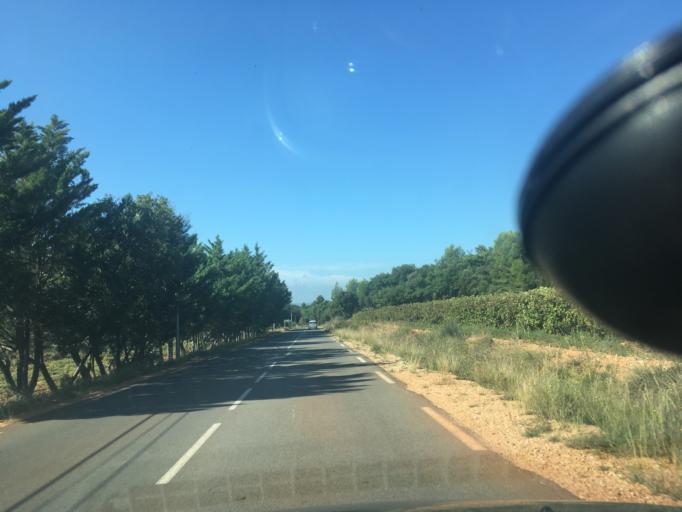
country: FR
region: Provence-Alpes-Cote d'Azur
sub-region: Departement du Var
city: Barjols
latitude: 43.6032
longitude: 6.0506
